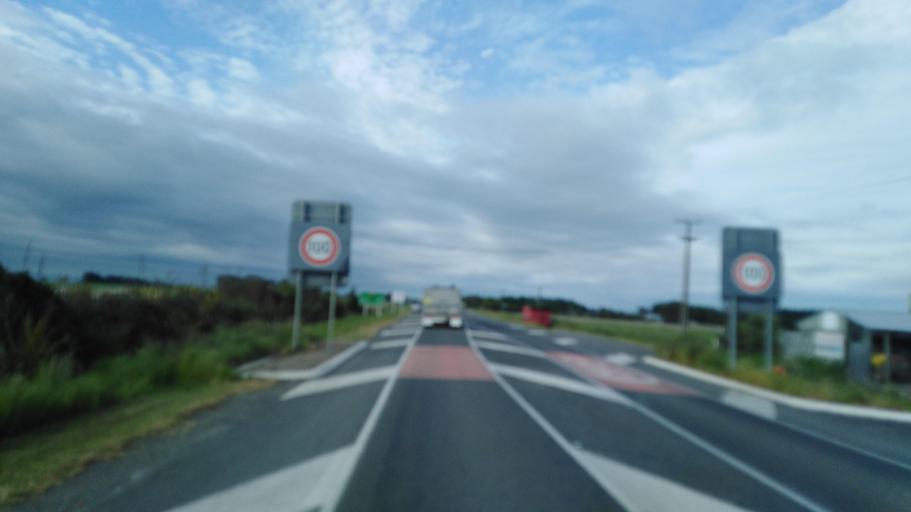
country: NZ
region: Manawatu-Wanganui
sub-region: Rangitikei District
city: Bulls
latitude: -40.2220
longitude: 175.4225
